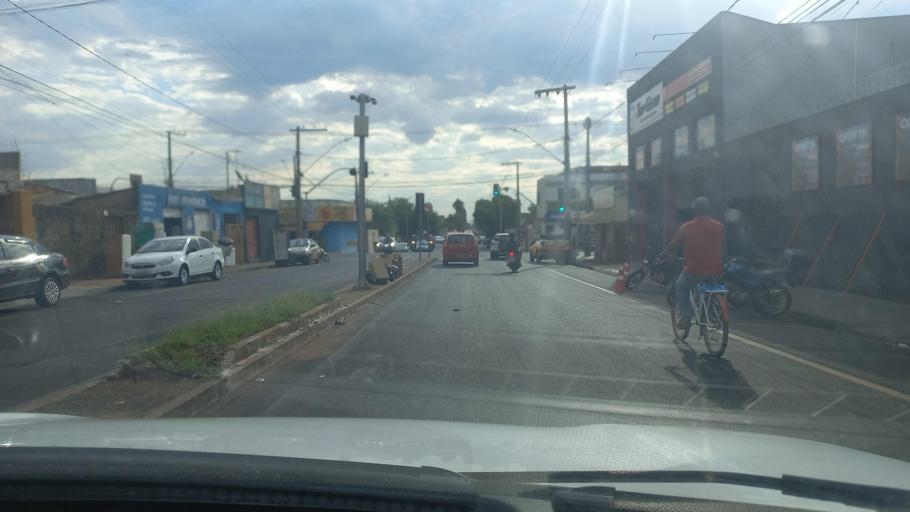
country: BR
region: Minas Gerais
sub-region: Uberaba
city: Uberaba
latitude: -19.7681
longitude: -47.9240
